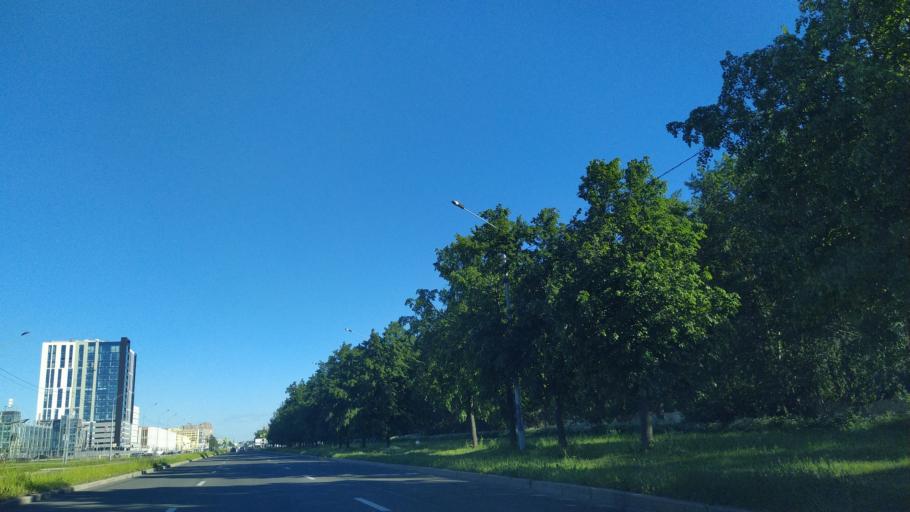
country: RU
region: St.-Petersburg
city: Kupchino
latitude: 59.8870
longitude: 30.3837
